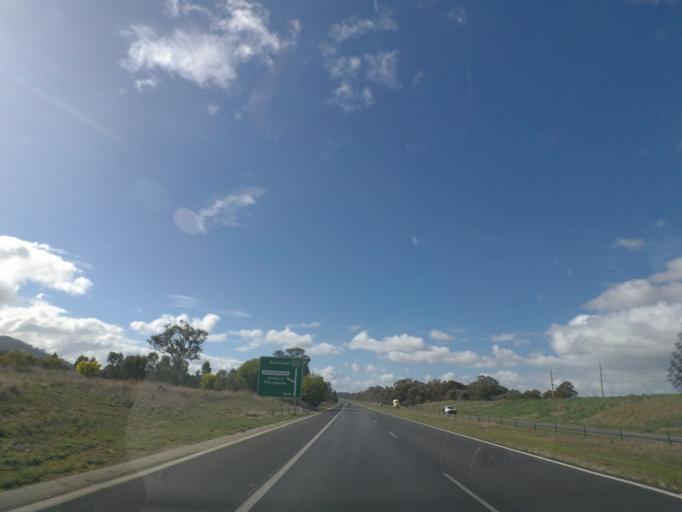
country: AU
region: New South Wales
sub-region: Albury Municipality
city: Lavington
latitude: -36.0503
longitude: 146.9617
